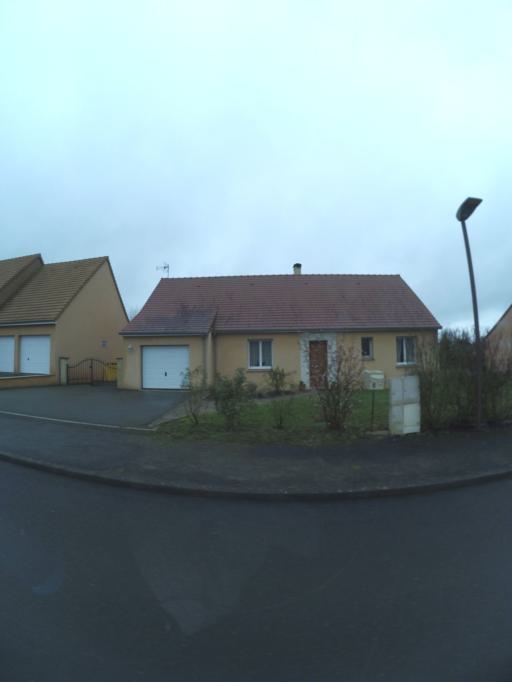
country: FR
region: Pays de la Loire
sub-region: Departement de la Sarthe
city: Saint-Saturnin
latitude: 48.0604
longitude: 0.1447
